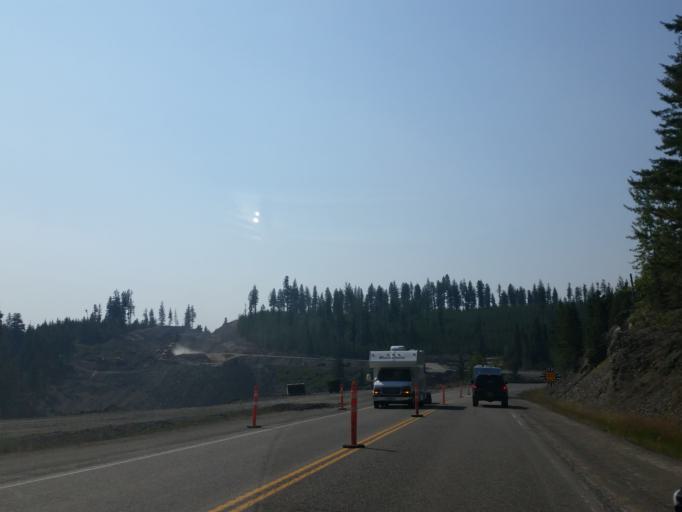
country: CA
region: British Columbia
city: Princeton
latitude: 49.2810
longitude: -120.5805
